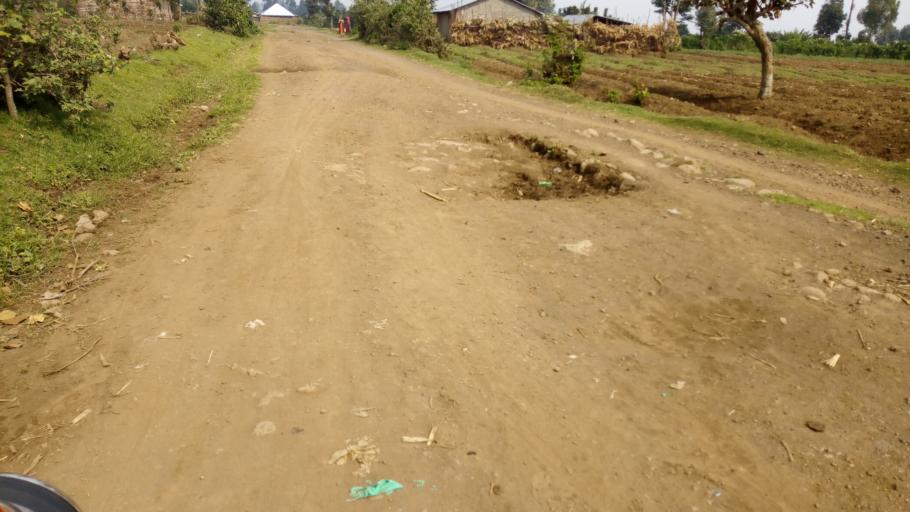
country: UG
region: Western Region
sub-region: Kisoro District
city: Kisoro
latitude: -1.3320
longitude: 29.6111
